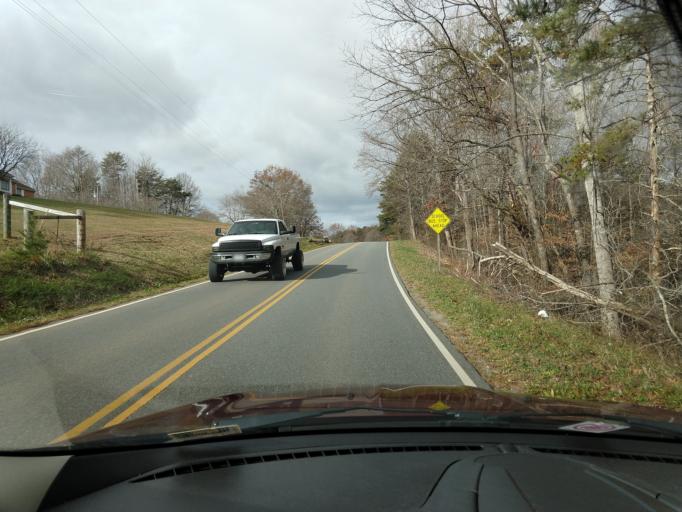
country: US
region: Virginia
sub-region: Franklin County
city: North Shore
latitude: 37.1922
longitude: -79.6726
